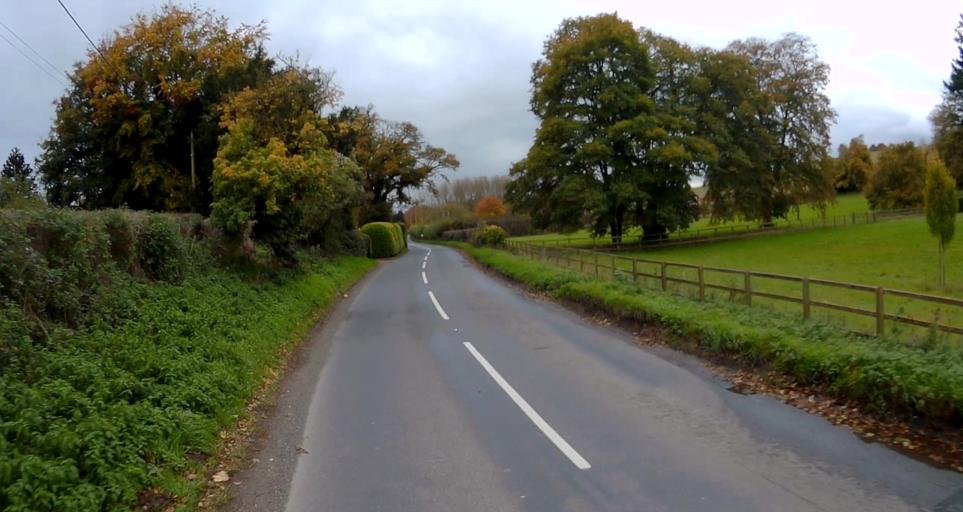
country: GB
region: England
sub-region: Hampshire
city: Basingstoke
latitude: 51.1815
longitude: -1.1275
